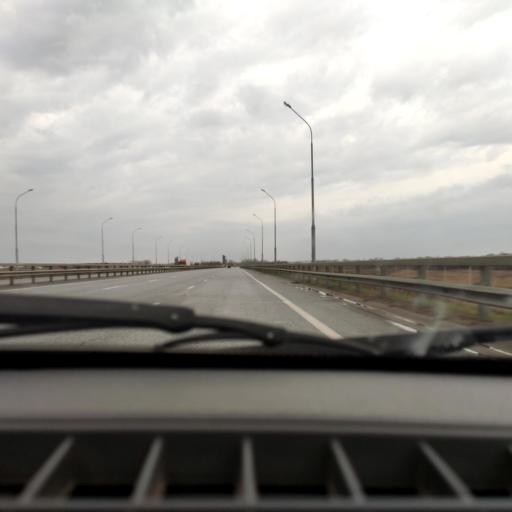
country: RU
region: Bashkortostan
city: Ufa
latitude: 54.6436
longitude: 55.9629
